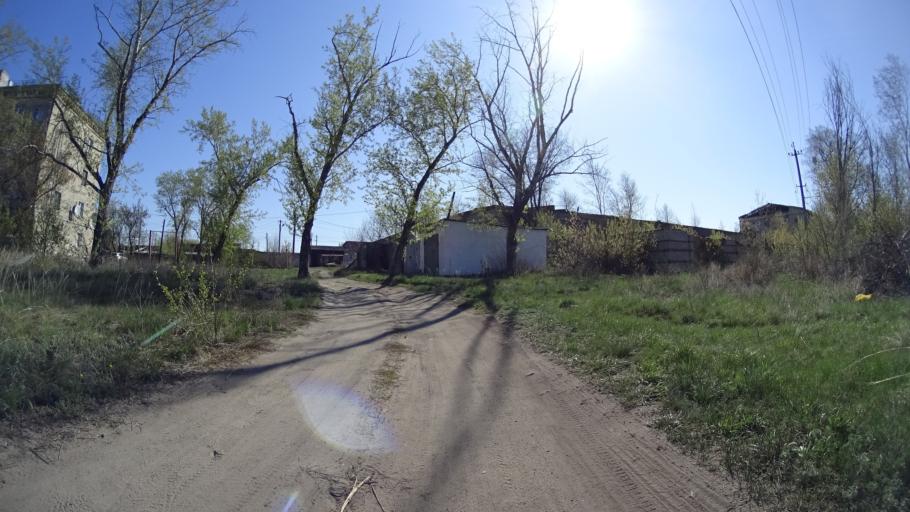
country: RU
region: Chelyabinsk
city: Troitsk
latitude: 54.0820
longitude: 61.5974
